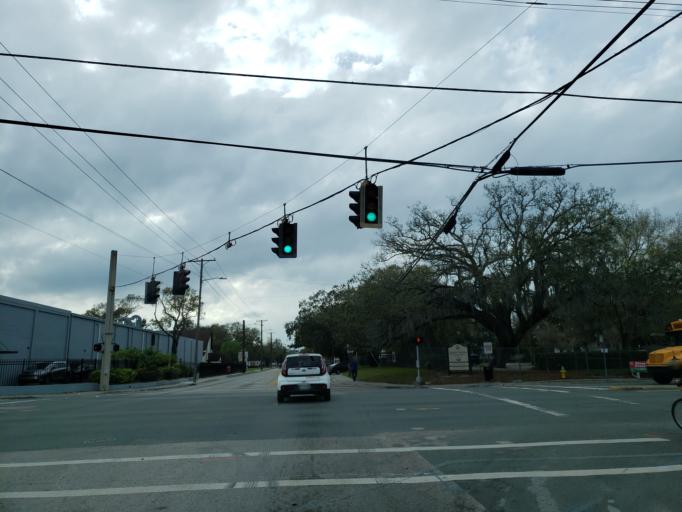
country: US
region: Florida
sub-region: Hillsborough County
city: East Lake-Orient Park
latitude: 27.9779
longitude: -82.4222
